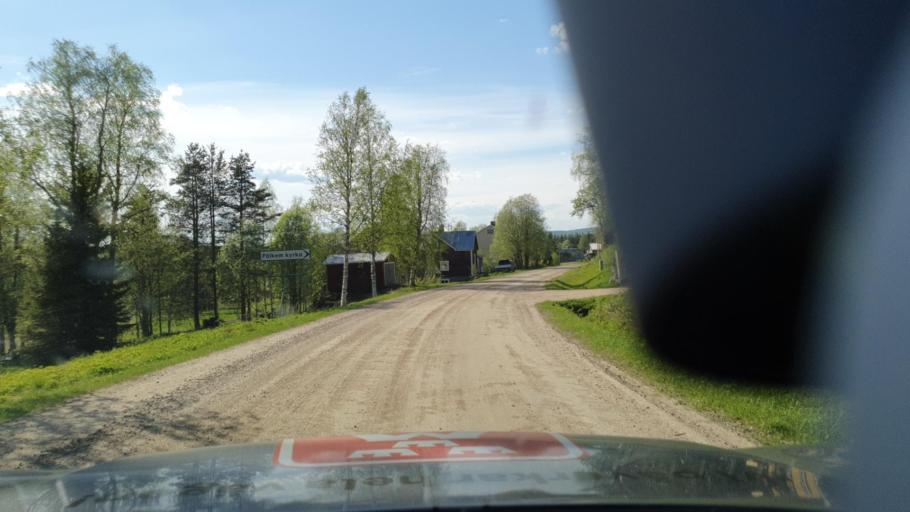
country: SE
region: Norrbotten
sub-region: Bodens Kommun
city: Boden
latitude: 66.3851
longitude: 21.6117
